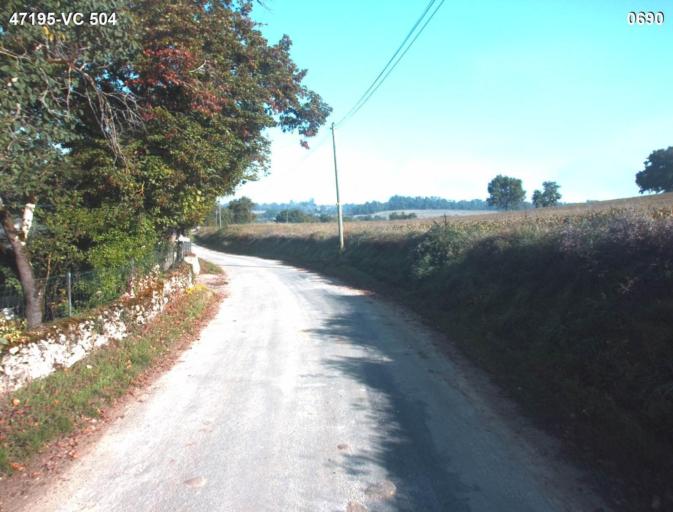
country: FR
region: Aquitaine
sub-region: Departement du Lot-et-Garonne
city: Nerac
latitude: 44.1536
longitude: 0.3342
